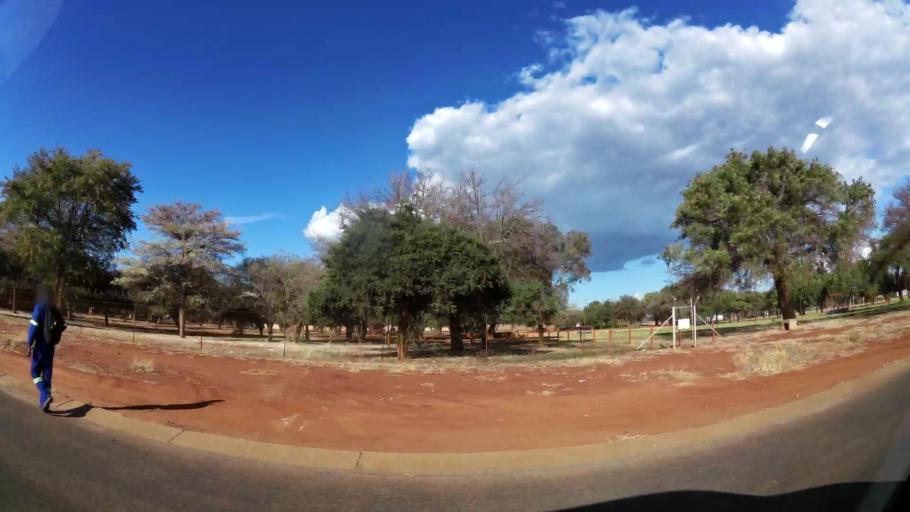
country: ZA
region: Limpopo
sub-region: Waterberg District Municipality
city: Mokopane
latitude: -24.1954
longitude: 29.0041
